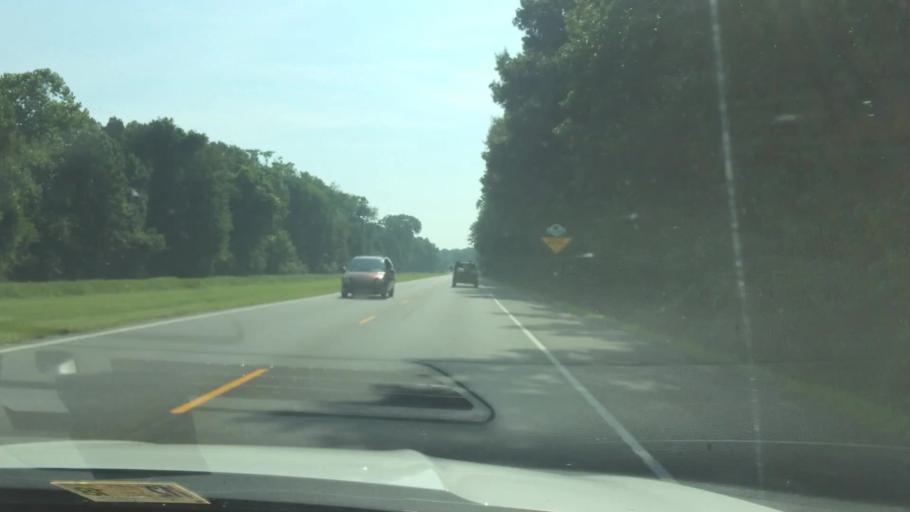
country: US
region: Virginia
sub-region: City of Poquoson
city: Poquoson
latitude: 37.1252
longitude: -76.4012
